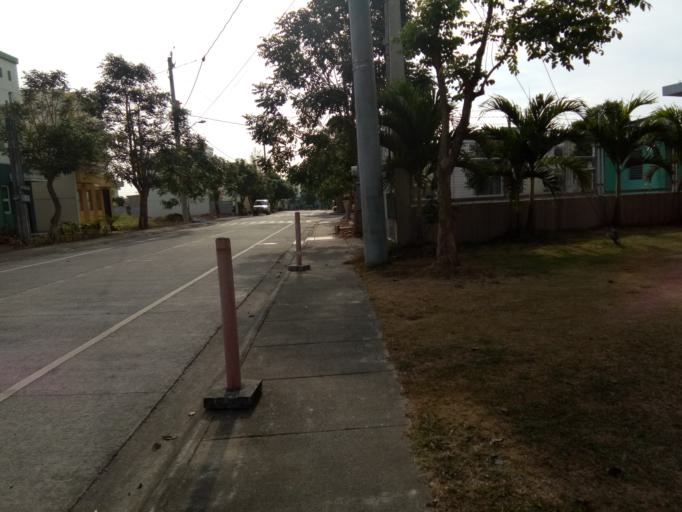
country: PH
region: Calabarzon
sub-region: Province of Cavite
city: Biga
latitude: 14.2775
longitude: 120.9707
